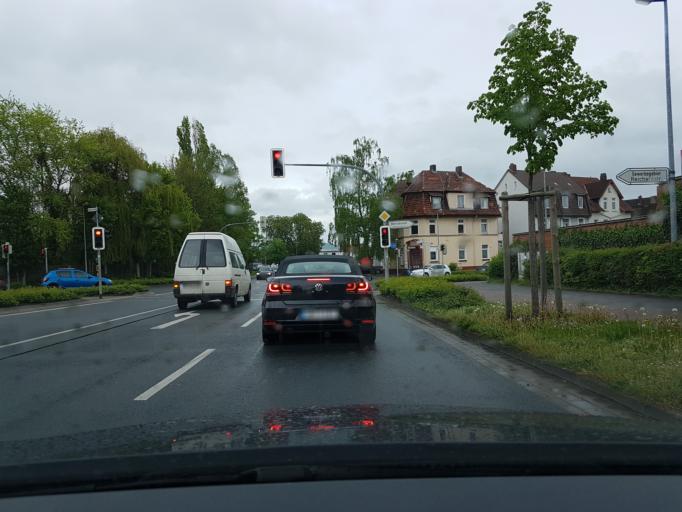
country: DE
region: Lower Saxony
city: Hameln
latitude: 52.0971
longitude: 9.3657
